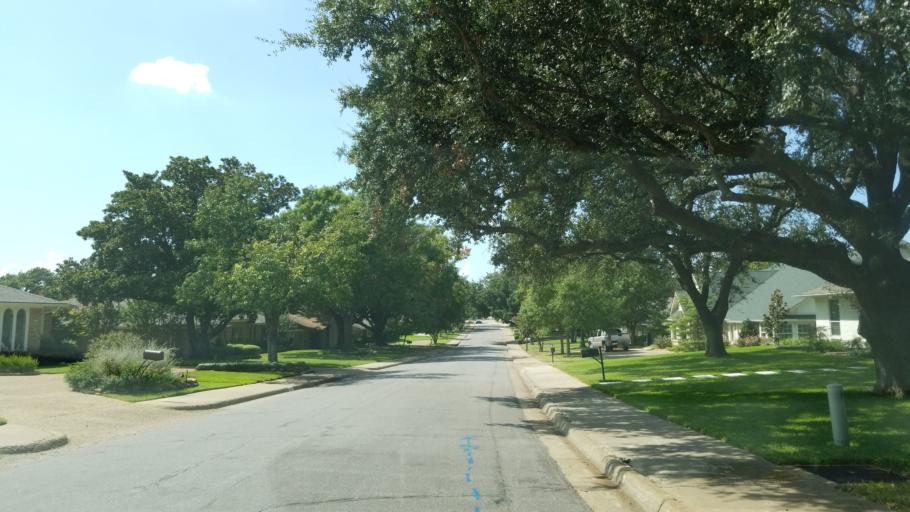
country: US
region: Texas
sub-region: Dallas County
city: Addison
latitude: 32.9559
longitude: -96.7894
